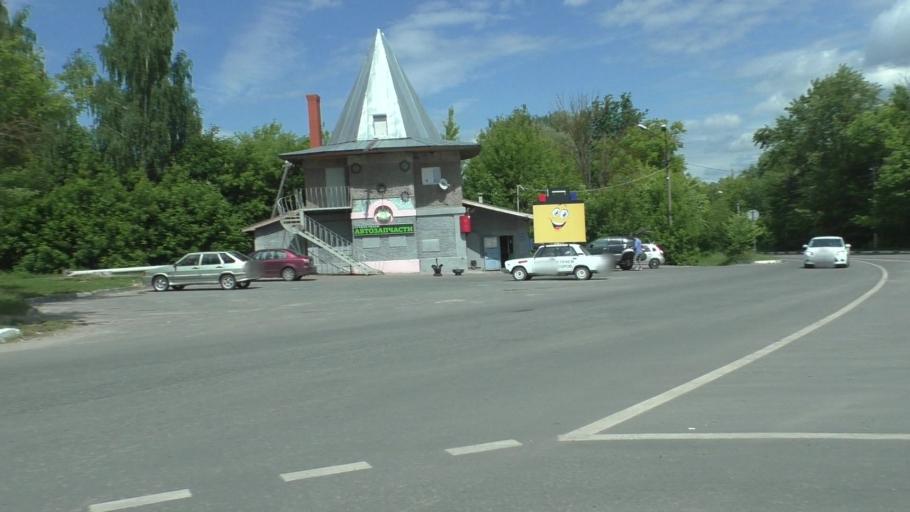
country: RU
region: Moskovskaya
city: Yegor'yevsk
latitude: 55.3871
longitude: 39.0337
